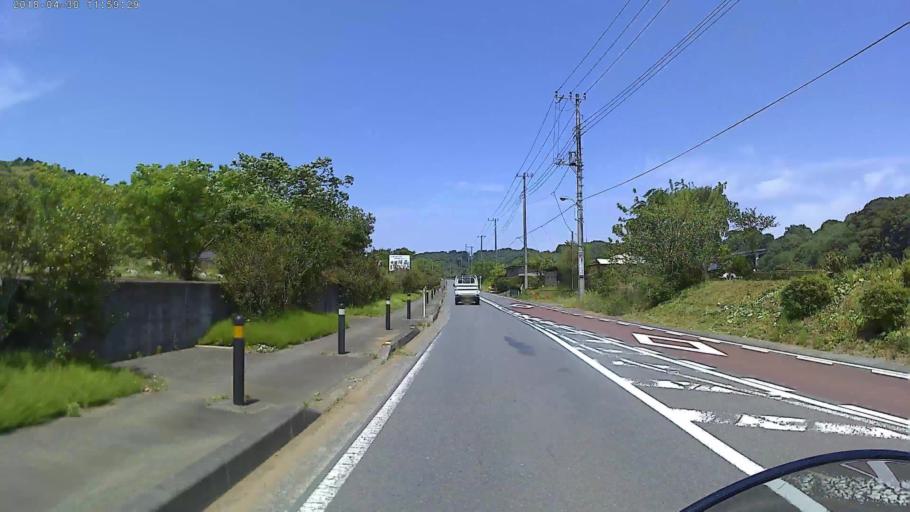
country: JP
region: Kanagawa
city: Zama
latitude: 35.5075
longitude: 139.3285
